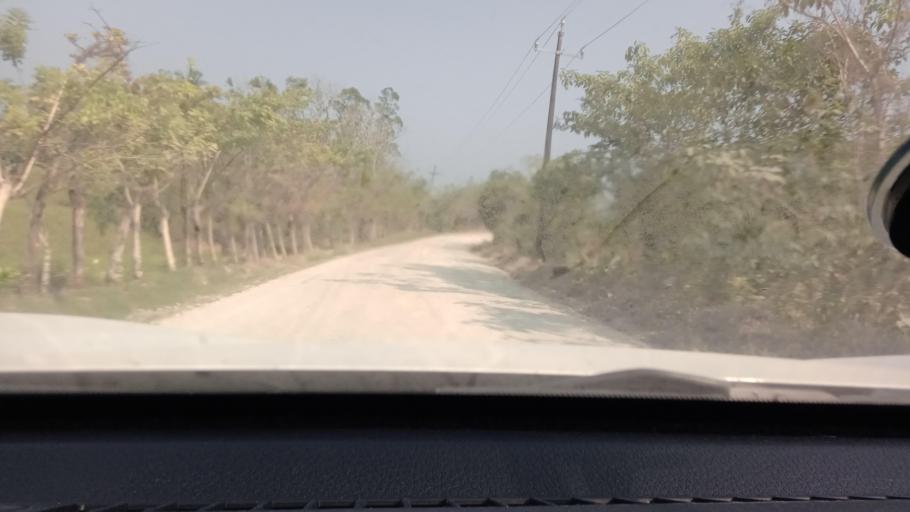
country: MX
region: Tabasco
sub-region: Huimanguillo
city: Francisco Rueda
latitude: 17.6195
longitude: -93.9415
